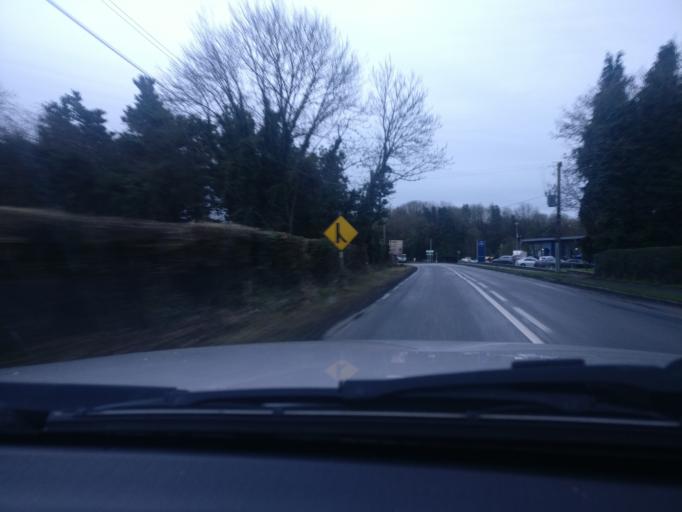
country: IE
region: Leinster
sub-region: An Mhi
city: Navan
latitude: 53.6605
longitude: -6.7236
